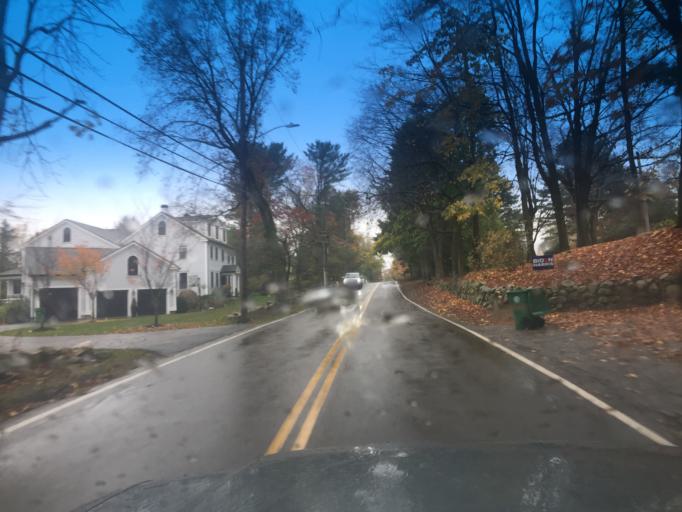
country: US
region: Massachusetts
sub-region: Norfolk County
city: Westwood
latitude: 42.2200
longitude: -71.2024
